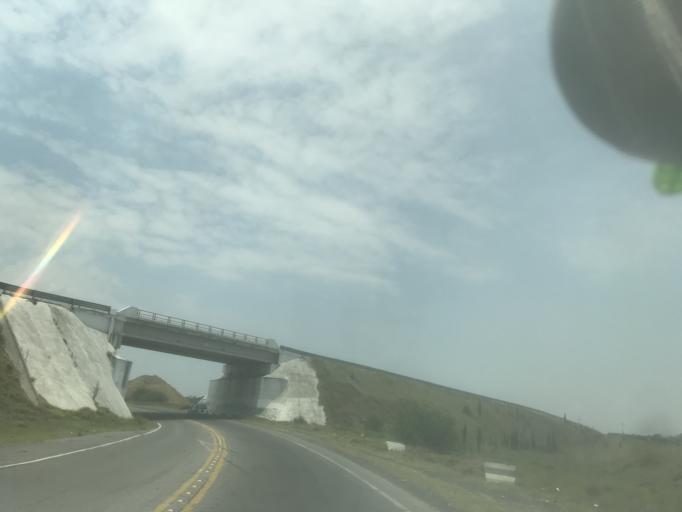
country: MX
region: Mexico
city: Ayapango
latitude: 19.1166
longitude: -98.7840
